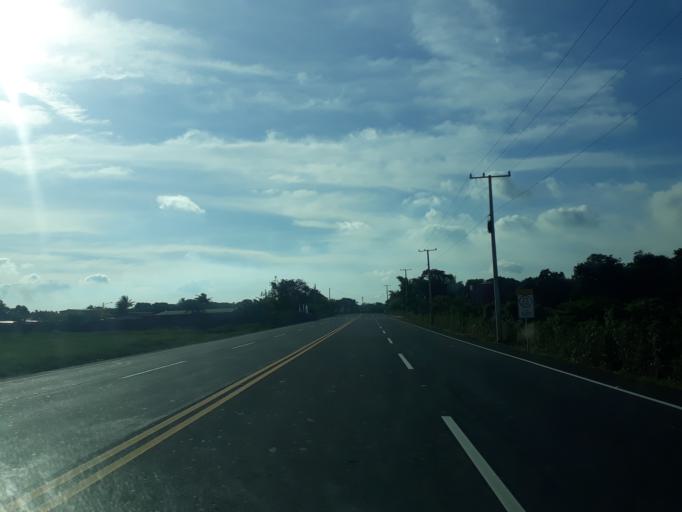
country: NI
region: Carazo
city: Diriamba
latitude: 11.9056
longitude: -86.2596
